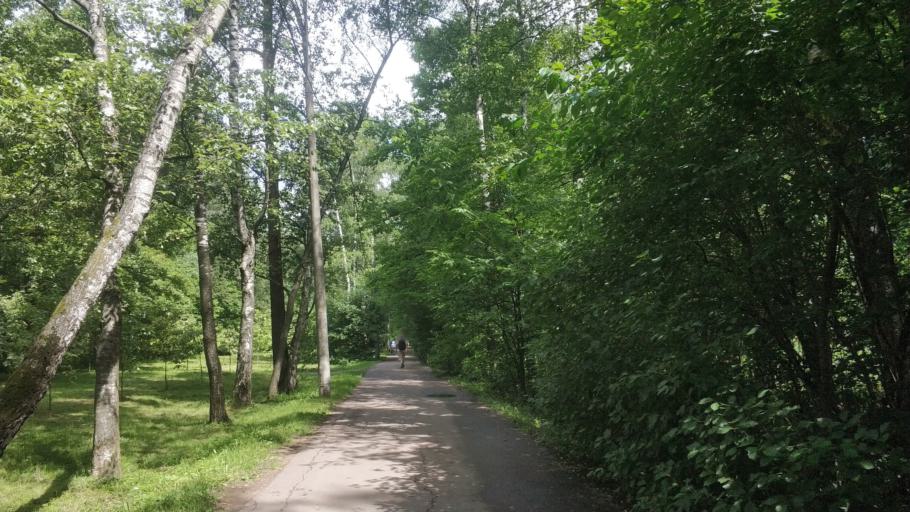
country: RU
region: Moscow
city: Perovo
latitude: 55.7281
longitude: 37.8008
